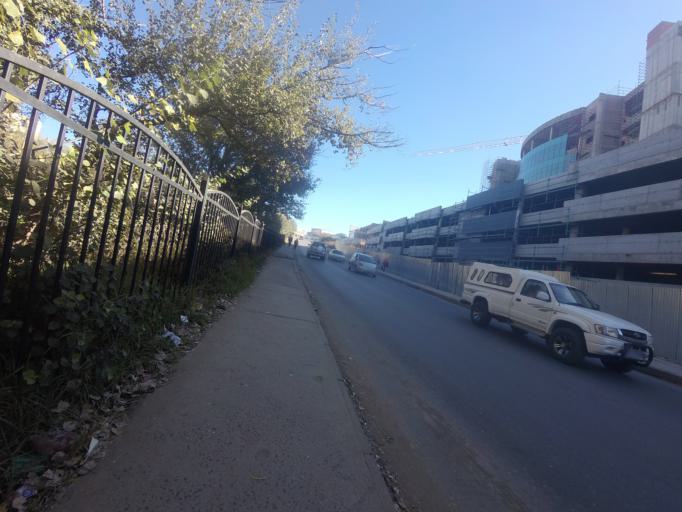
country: LS
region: Maseru
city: Maseru
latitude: -29.3136
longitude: 27.4894
